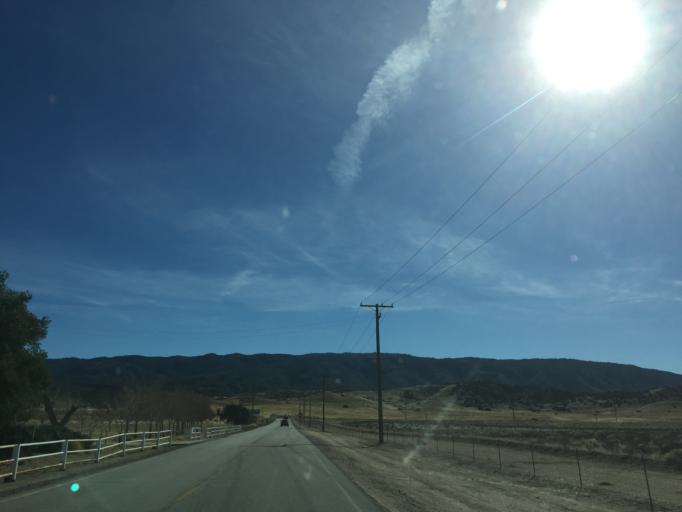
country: US
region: California
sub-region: Kern County
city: Lebec
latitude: 34.7868
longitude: -118.6611
